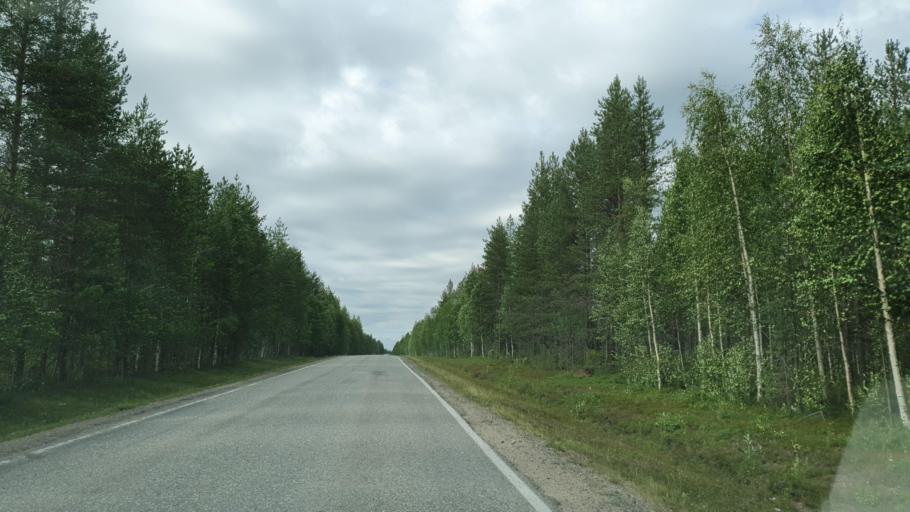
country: FI
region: Lapland
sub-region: Tunturi-Lappi
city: Kittilae
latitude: 67.6124
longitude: 25.3075
